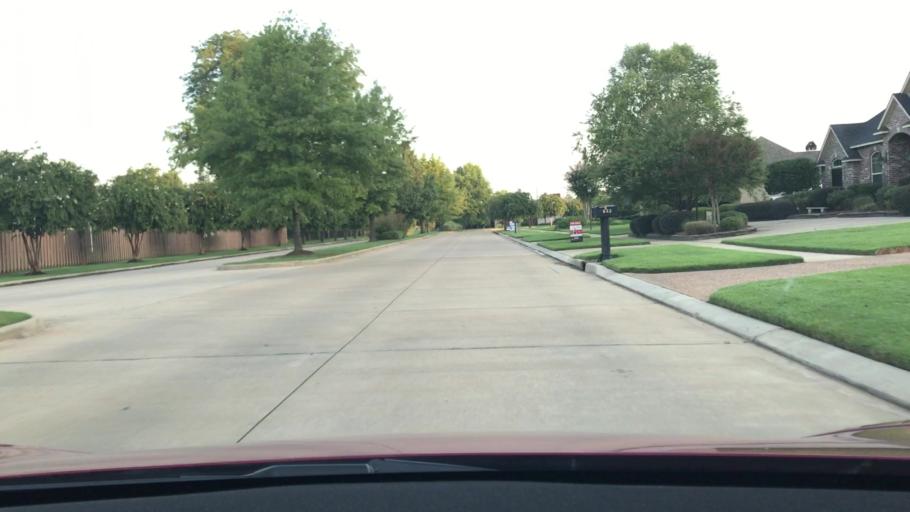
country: US
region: Louisiana
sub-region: Bossier Parish
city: Bossier City
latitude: 32.3984
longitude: -93.7093
